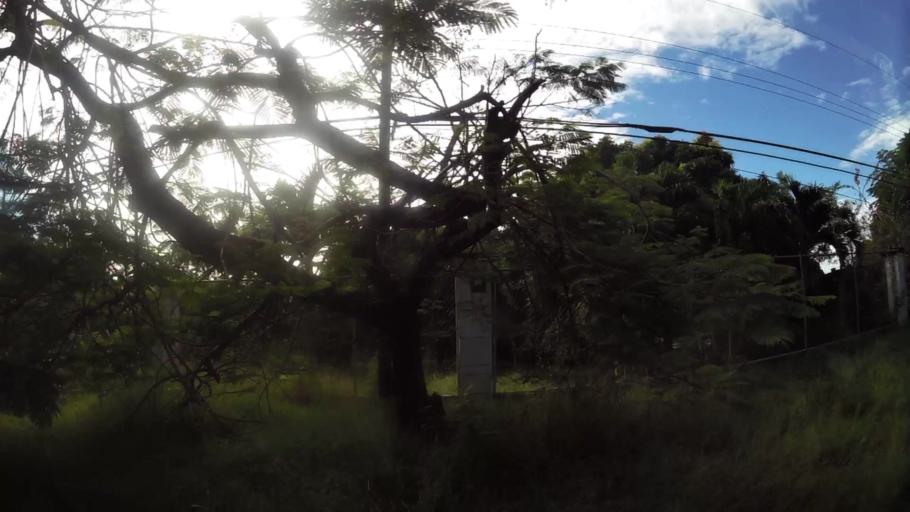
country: PA
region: Panama
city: Nueva Gorgona
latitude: 8.5296
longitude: -79.8857
